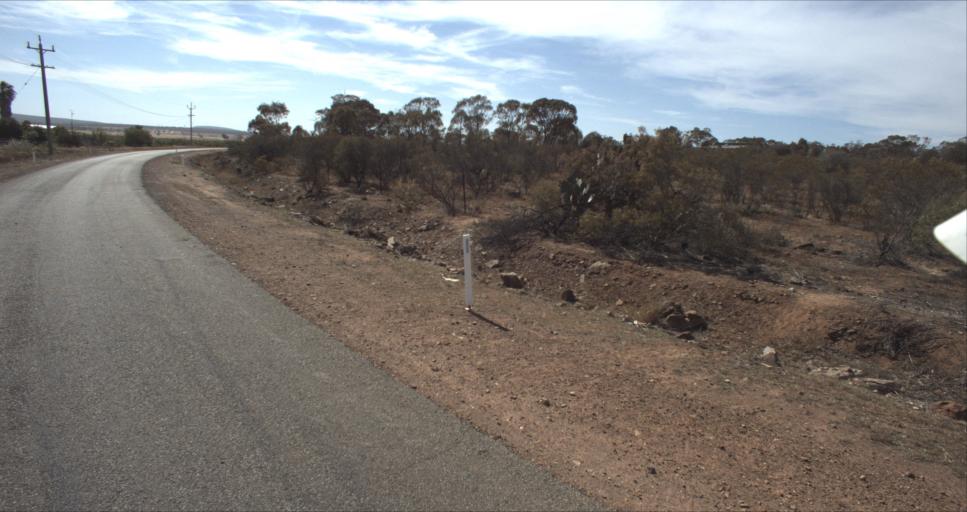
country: AU
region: New South Wales
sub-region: Leeton
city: Leeton
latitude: -34.5772
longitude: 146.4798
